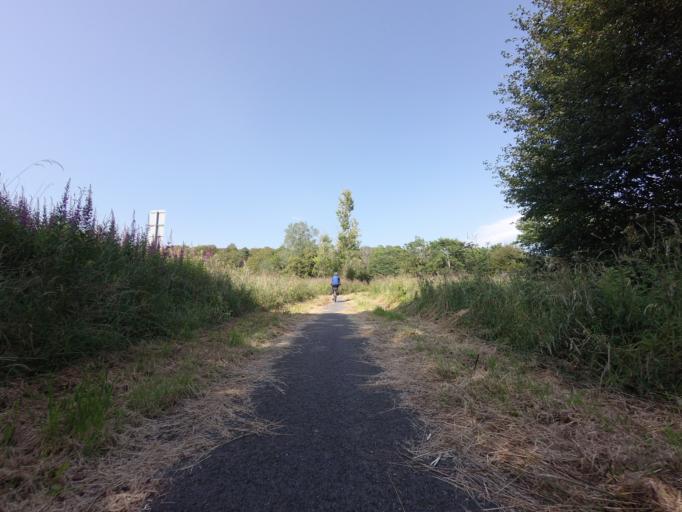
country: GB
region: Scotland
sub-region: Highland
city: Evanton
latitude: 57.6718
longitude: -4.3213
